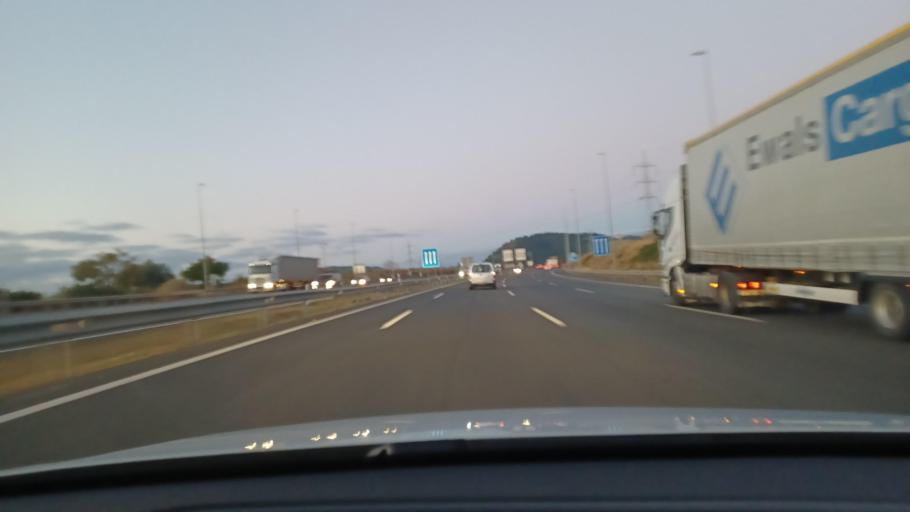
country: ES
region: Valencia
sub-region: Provincia de Valencia
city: Sagunto
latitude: 39.6980
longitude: -0.2731
